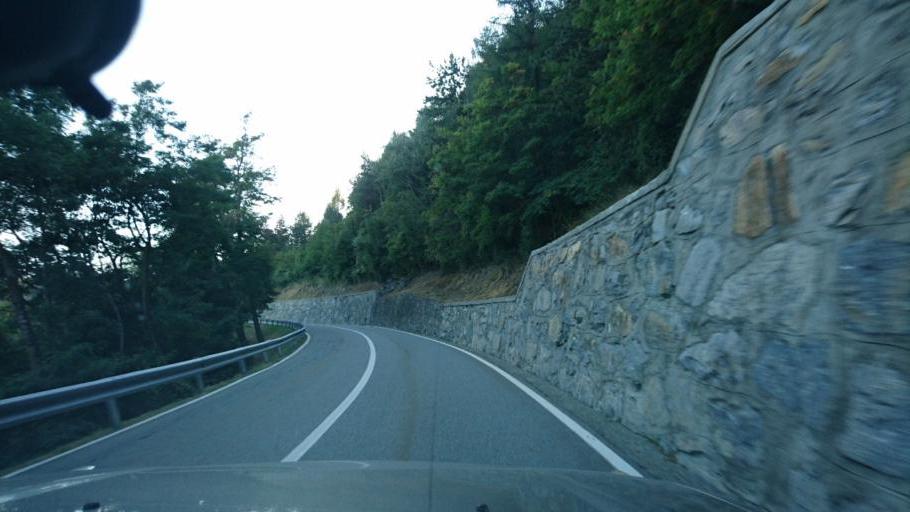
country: IT
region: Aosta Valley
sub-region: Valle d'Aosta
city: Saint-Nicolas
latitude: 45.7146
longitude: 7.1774
